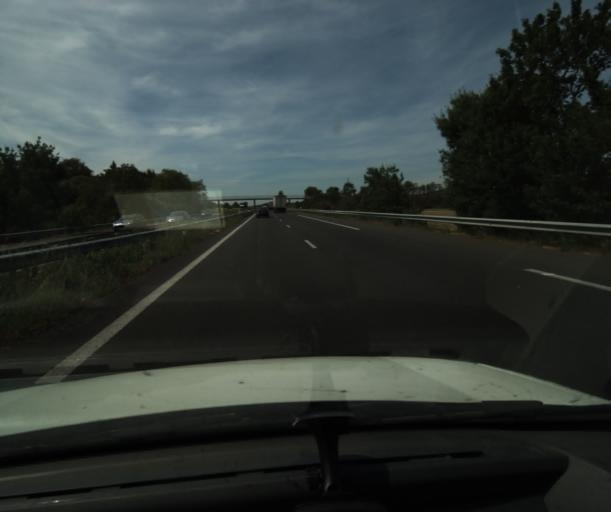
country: FR
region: Midi-Pyrenees
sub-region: Departement de la Haute-Garonne
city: Avignonet-Lauragais
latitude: 43.3311
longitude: 1.8460
